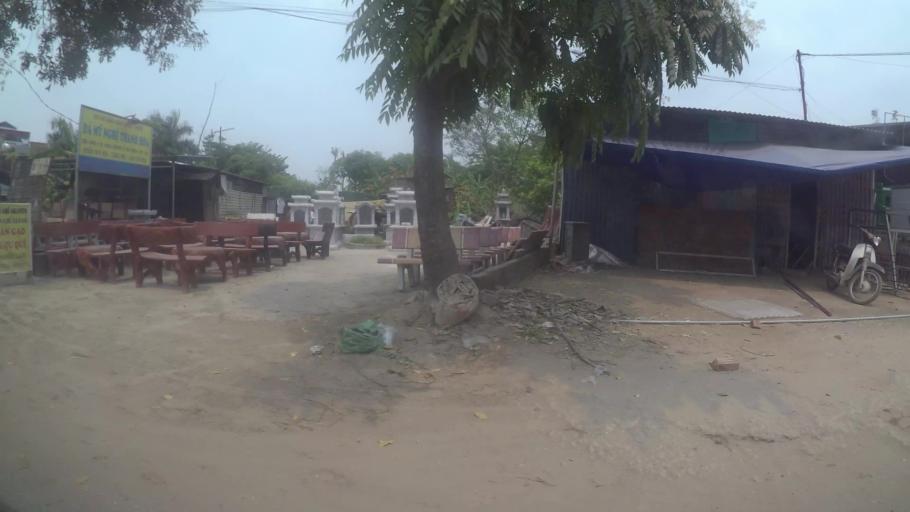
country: VN
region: Ha Noi
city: Cau Dien
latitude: 21.0275
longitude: 105.7410
